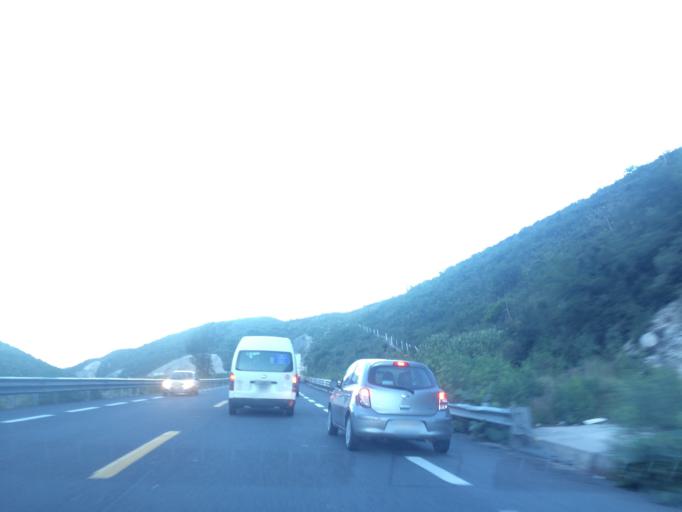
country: MX
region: Puebla
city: Chapuco
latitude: 18.6464
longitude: -97.4545
